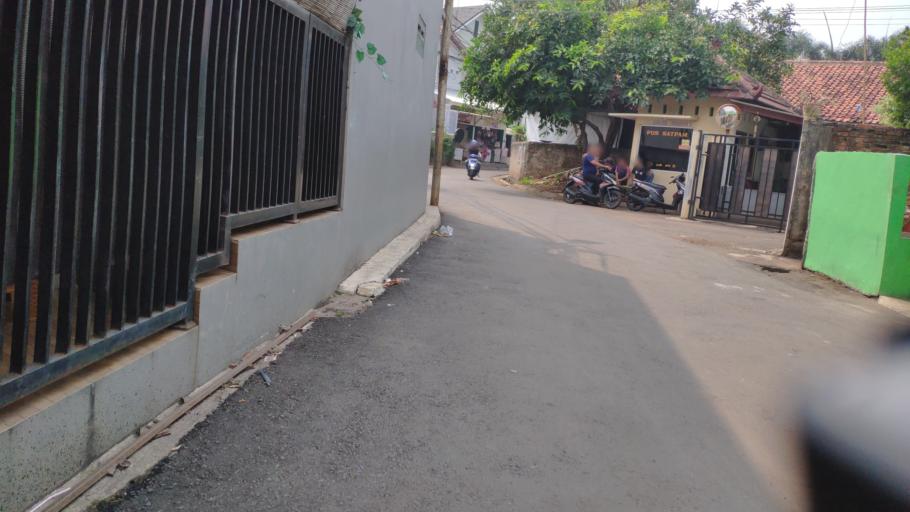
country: ID
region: West Java
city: Depok
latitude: -6.3209
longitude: 106.8214
